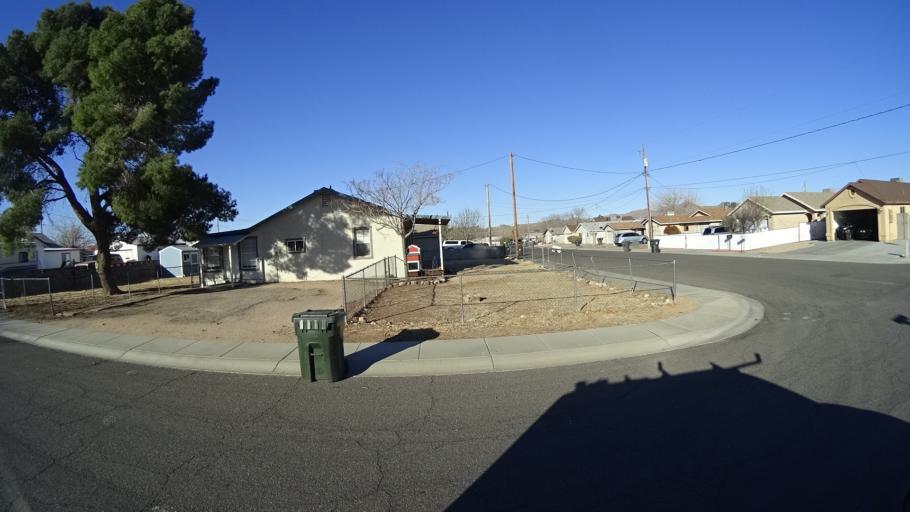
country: US
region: Arizona
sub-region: Mohave County
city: Kingman
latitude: 35.1998
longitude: -114.0180
